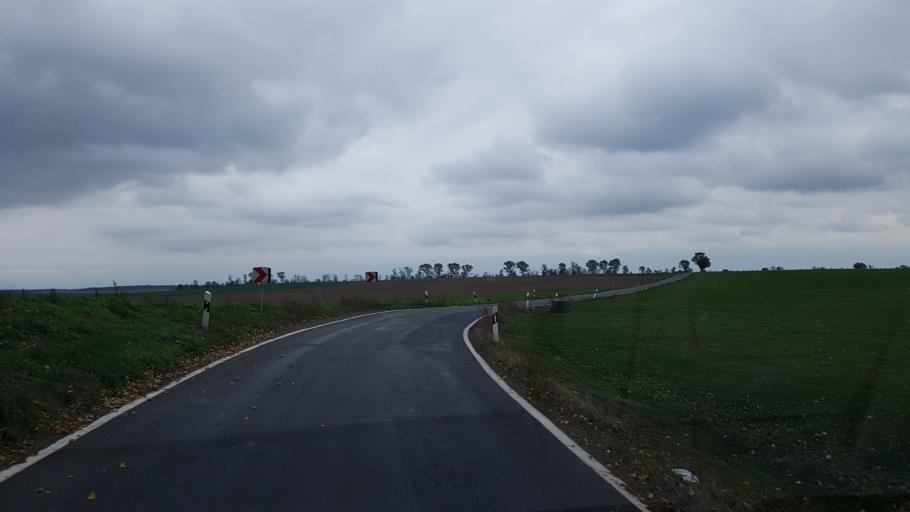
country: DE
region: Saxony
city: Dahlen
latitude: 51.3799
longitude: 12.9513
